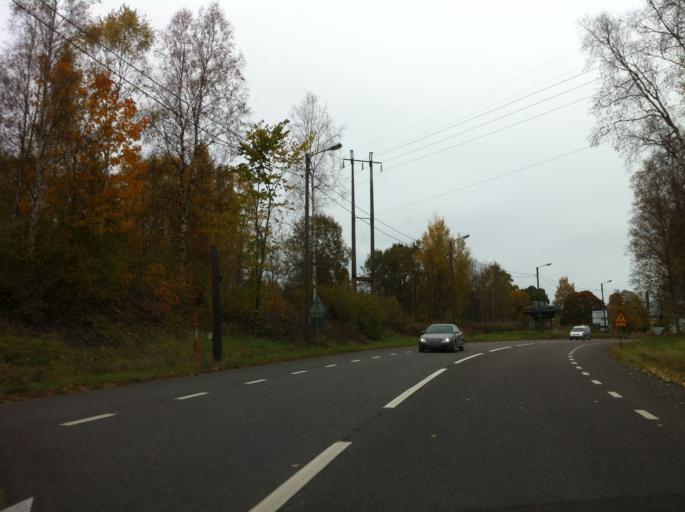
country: SE
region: Dalarna
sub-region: Ludvika Kommun
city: Grangesberg
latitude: 60.0647
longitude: 14.9860
